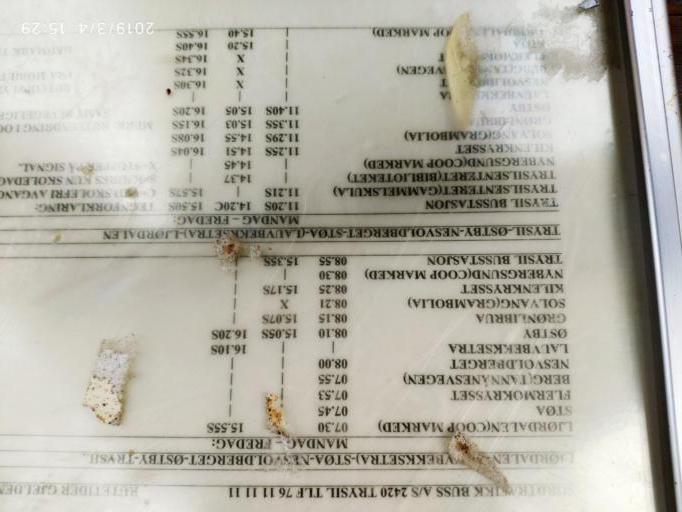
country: NO
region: Hedmark
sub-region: Trysil
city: Innbygda
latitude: 61.2544
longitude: 12.5312
